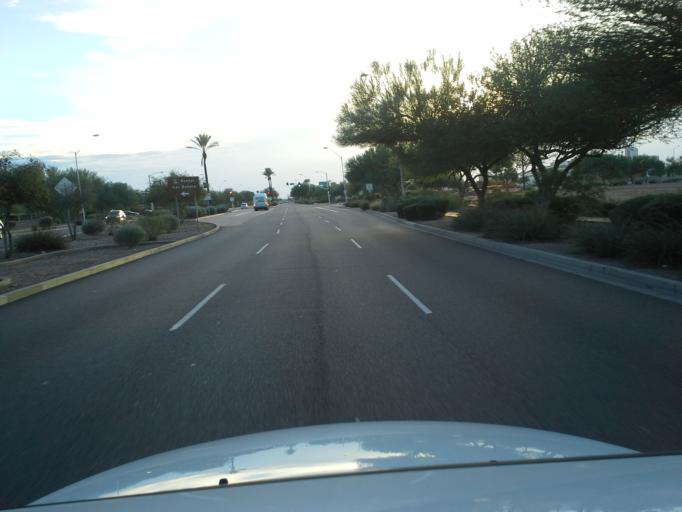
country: US
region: Arizona
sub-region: Maricopa County
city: Phoenix
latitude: 33.4370
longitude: -112.0413
